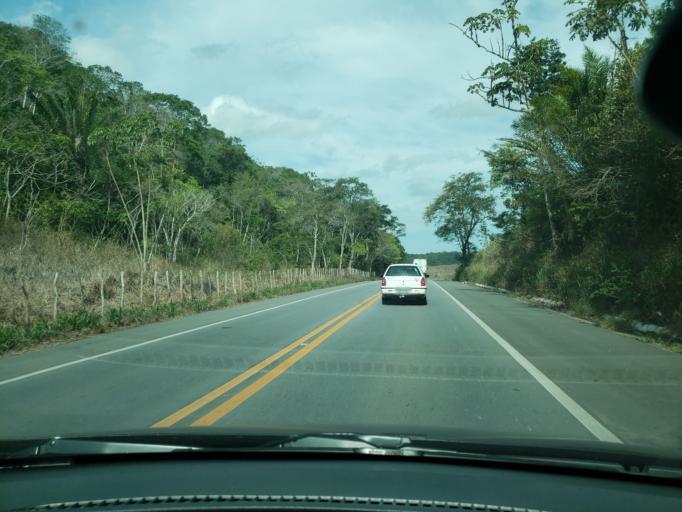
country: BR
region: Alagoas
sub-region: Murici
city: Murici
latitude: -9.3311
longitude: -35.9109
